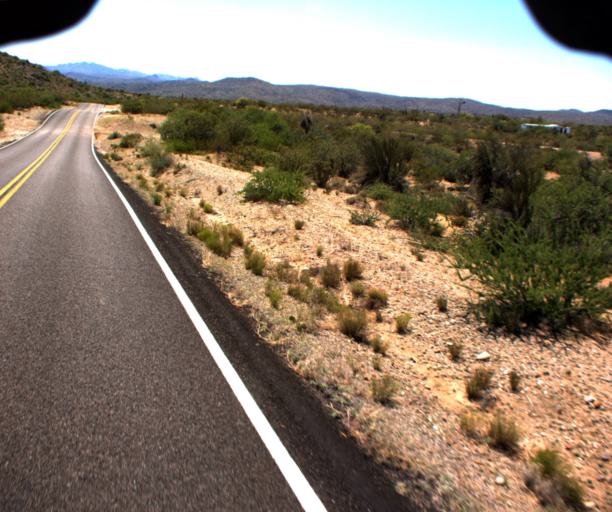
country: US
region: Arizona
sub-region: Yavapai County
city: Bagdad
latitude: 34.4816
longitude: -113.1941
